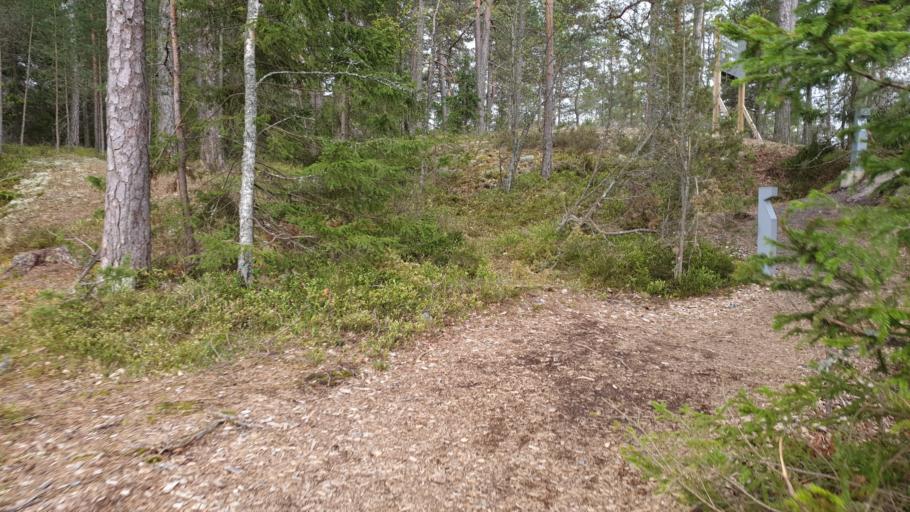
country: SE
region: Stockholm
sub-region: Varmdo Kommun
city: Gustavsberg
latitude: 59.3063
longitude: 18.3477
